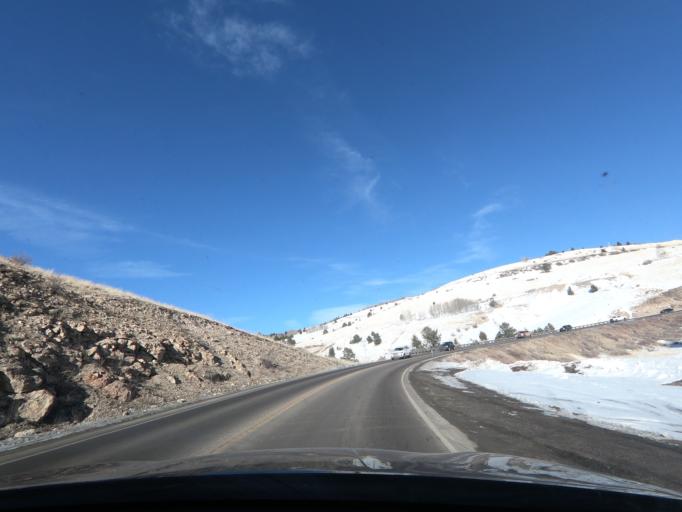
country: US
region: Colorado
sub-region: Teller County
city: Cripple Creek
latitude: 38.7548
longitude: -105.1671
